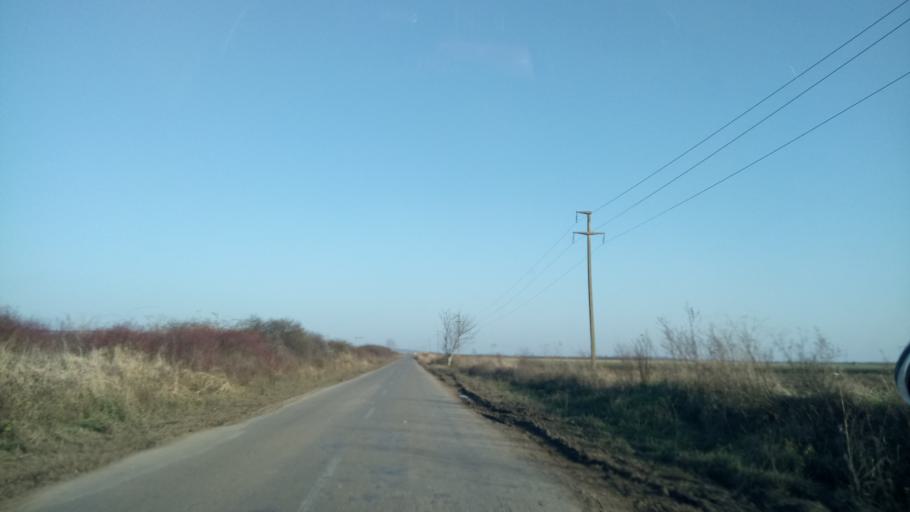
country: RS
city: Krcedin
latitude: 45.1407
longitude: 20.1656
